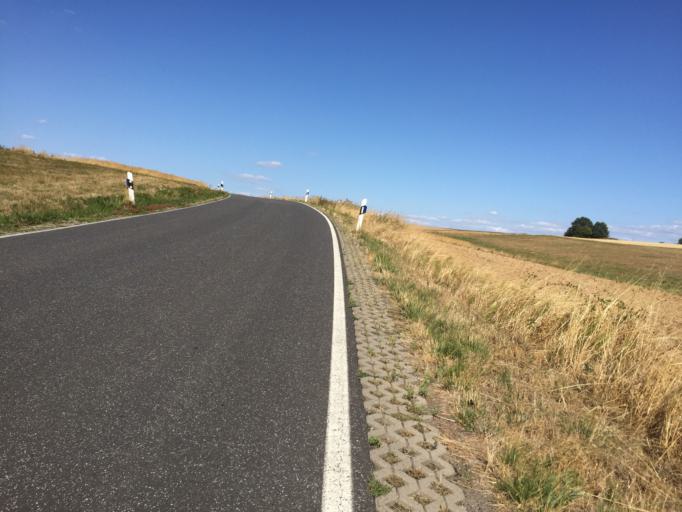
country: DE
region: Hesse
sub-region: Regierungsbezirk Giessen
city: Grunberg
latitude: 50.6060
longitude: 8.9281
